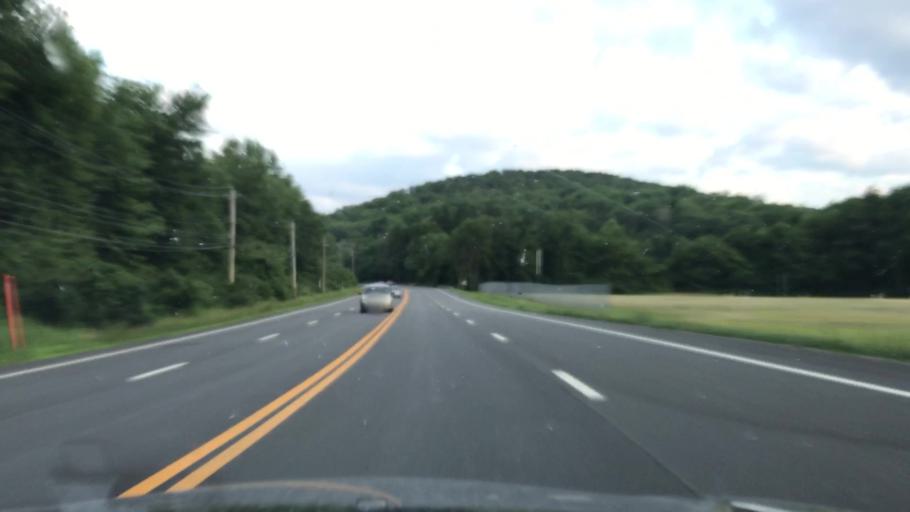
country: US
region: New York
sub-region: Rockland County
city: Sloatsburg
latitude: 41.2233
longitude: -74.1882
